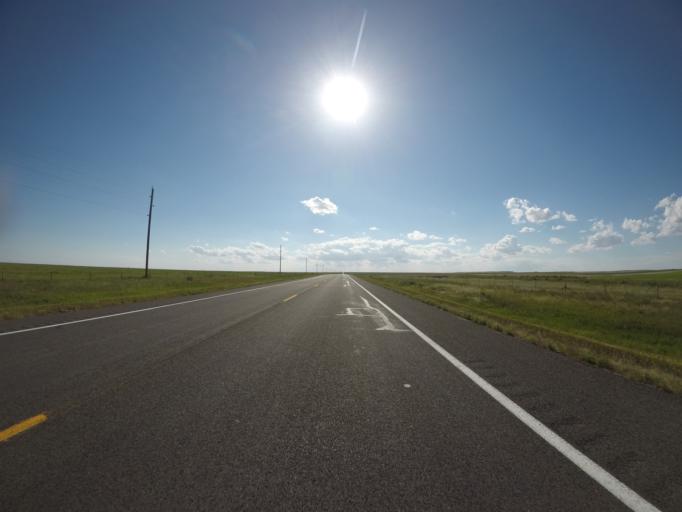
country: US
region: Colorado
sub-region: Morgan County
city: Fort Morgan
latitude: 40.6104
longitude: -103.7361
